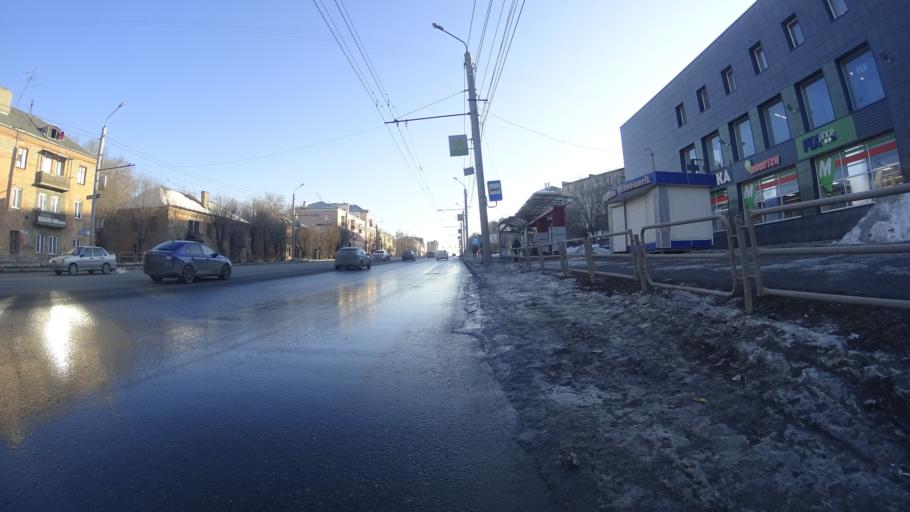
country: RU
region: Chelyabinsk
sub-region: Gorod Chelyabinsk
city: Chelyabinsk
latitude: 55.1880
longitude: 61.3865
